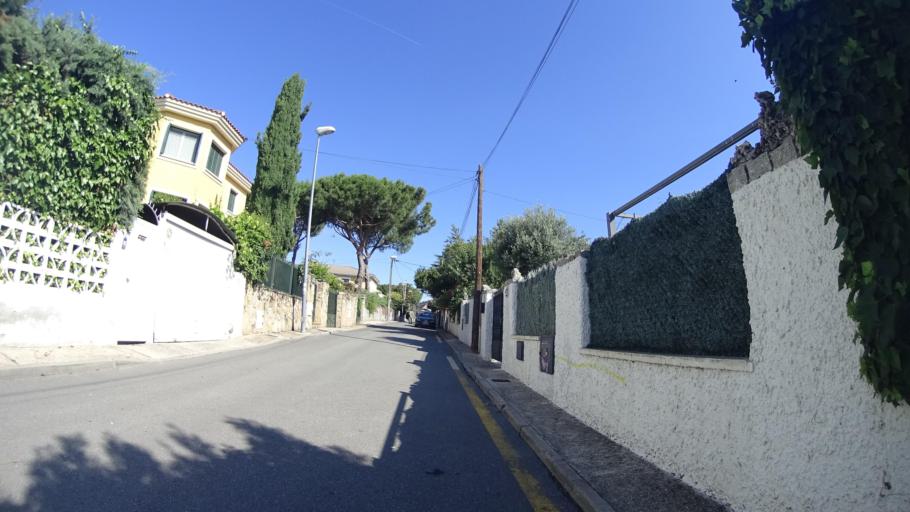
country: ES
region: Madrid
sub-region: Provincia de Madrid
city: Las Matas
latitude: 40.5480
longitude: -3.8912
